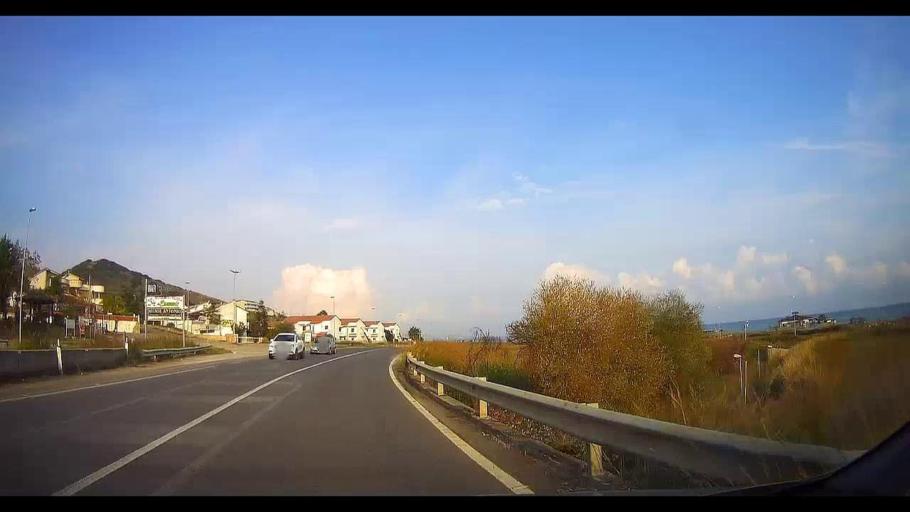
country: IT
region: Calabria
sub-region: Provincia di Cosenza
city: Cariati
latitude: 39.5259
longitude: 16.8897
